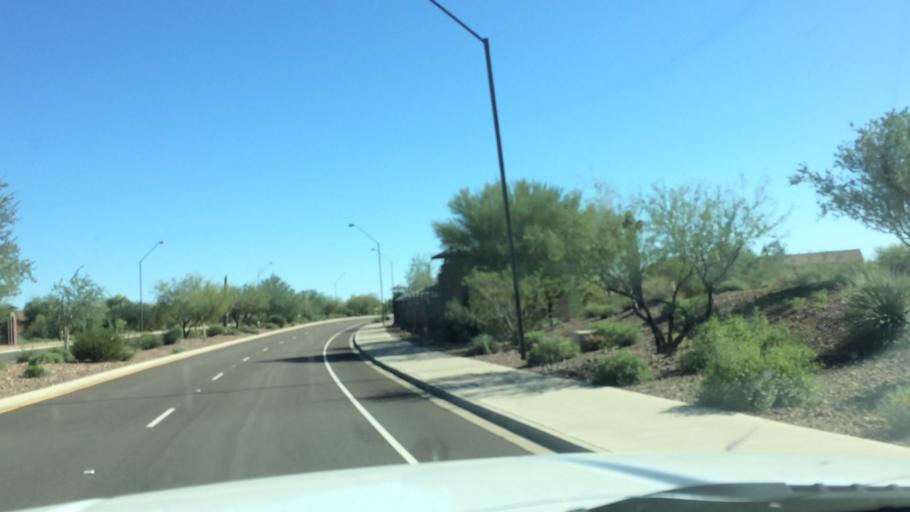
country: US
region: Arizona
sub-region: Maricopa County
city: Anthem
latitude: 33.8572
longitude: -112.1067
